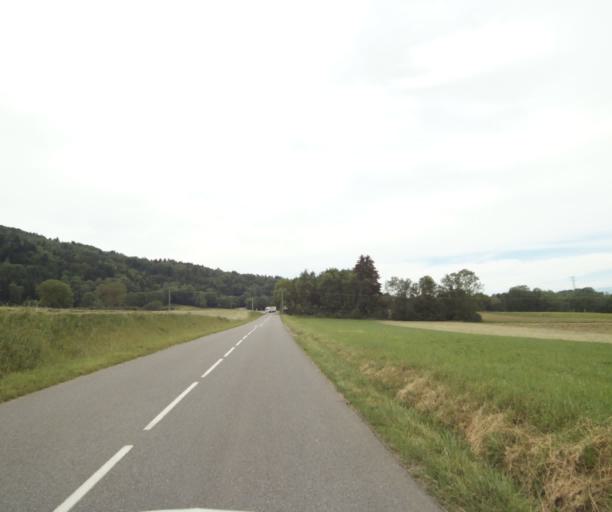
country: FR
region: Rhone-Alpes
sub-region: Departement de la Haute-Savoie
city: Allinges
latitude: 46.3087
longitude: 6.4751
